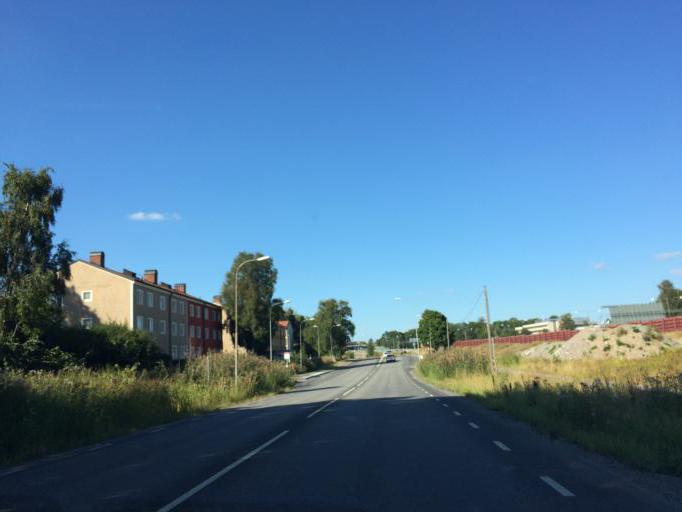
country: SE
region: Stockholm
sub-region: Upplands Vasby Kommun
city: Upplands Vaesby
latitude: 59.4800
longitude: 17.9184
